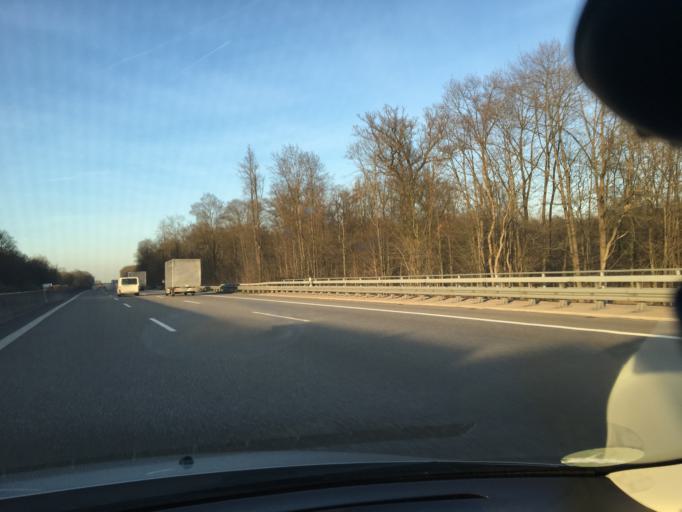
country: DE
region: Baden-Wuerttemberg
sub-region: Freiburg Region
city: Renchen
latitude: 48.5883
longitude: 7.9762
